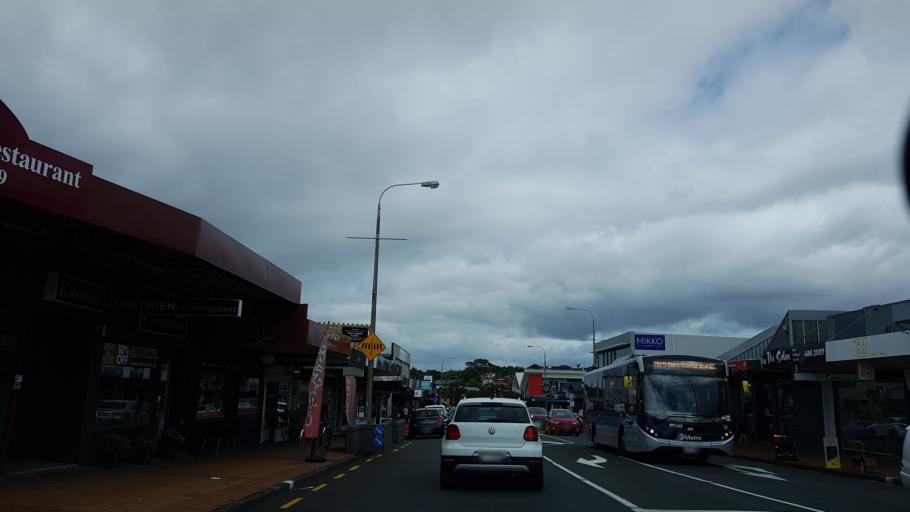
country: NZ
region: Auckland
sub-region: Auckland
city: North Shore
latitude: -36.7730
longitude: 174.7664
